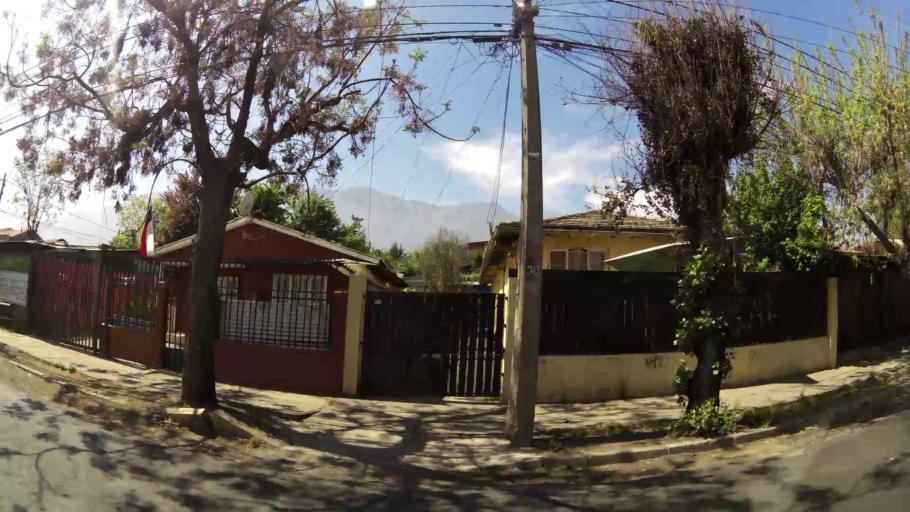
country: CL
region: Santiago Metropolitan
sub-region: Provincia de Santiago
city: Villa Presidente Frei, Nunoa, Santiago, Chile
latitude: -33.4752
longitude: -70.5339
